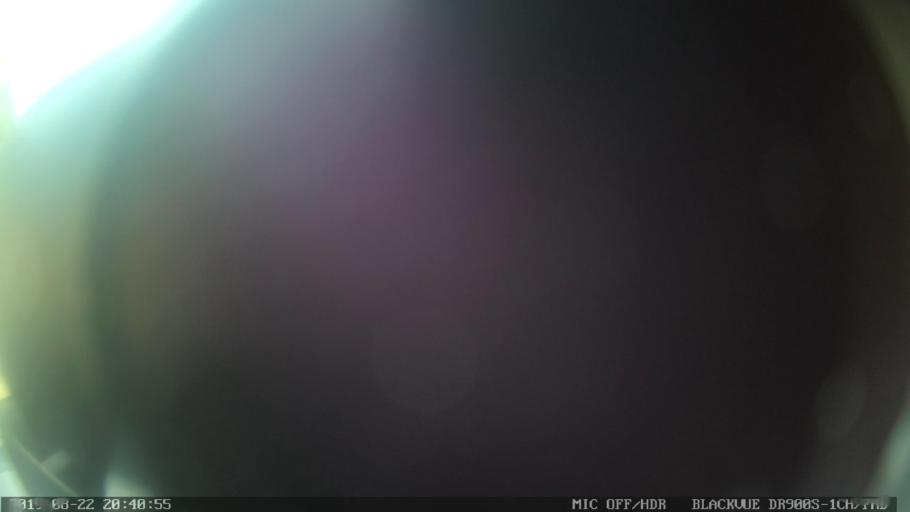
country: PT
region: Castelo Branco
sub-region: Proenca-A-Nova
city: Proenca-a-Nova
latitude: 39.6863
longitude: -7.7960
